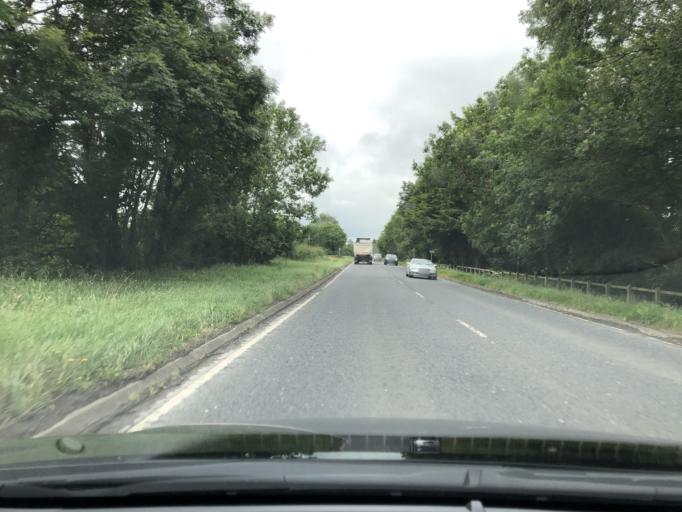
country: GB
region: Northern Ireland
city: Ballynahinch
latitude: 54.3427
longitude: -5.8437
